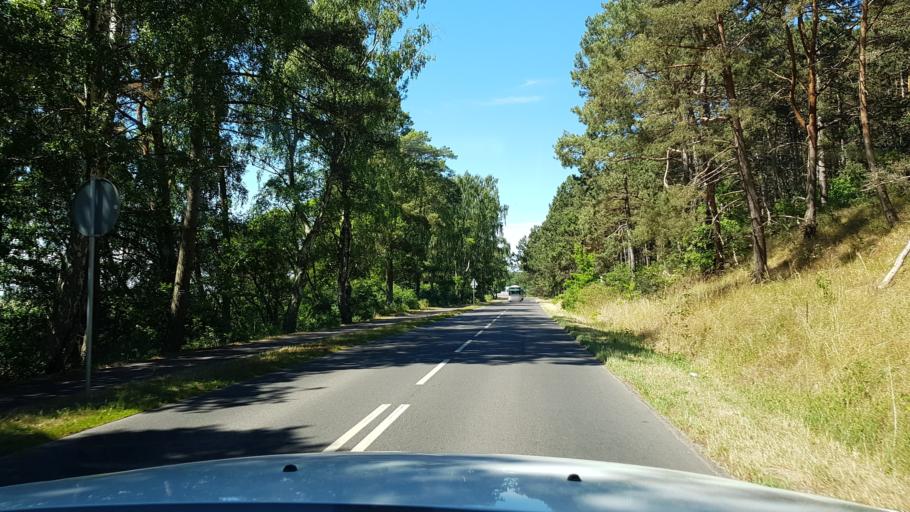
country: PL
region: West Pomeranian Voivodeship
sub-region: Powiat gryficki
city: Mrzezyno
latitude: 54.1539
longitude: 15.3671
